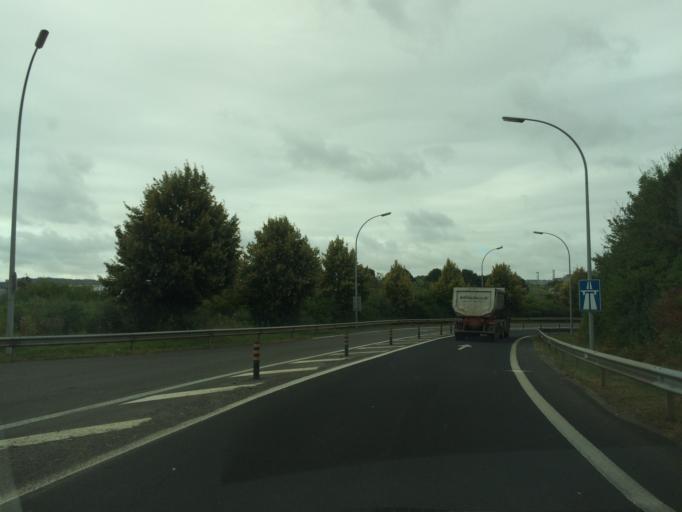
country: LU
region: Luxembourg
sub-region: Canton d'Esch-sur-Alzette
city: Esch-sur-Alzette
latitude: 49.5120
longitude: 5.9763
